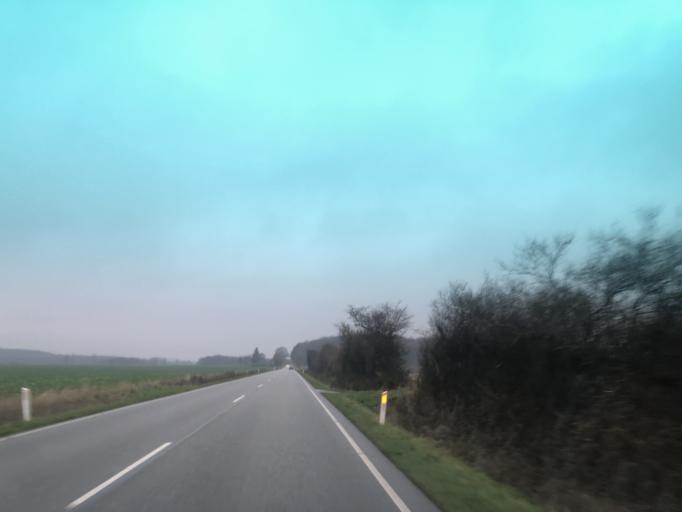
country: DK
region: South Denmark
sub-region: Nyborg Kommune
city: Ullerslev
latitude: 55.2453
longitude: 10.6602
